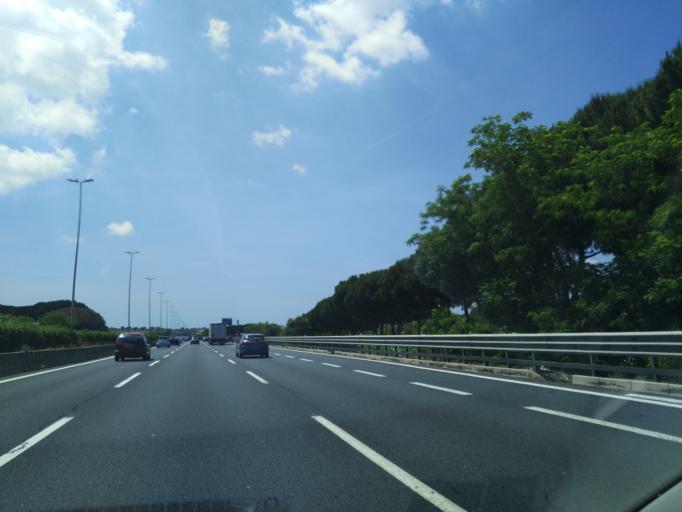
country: IT
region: Latium
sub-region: Citta metropolitana di Roma Capitale
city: Borgo Lotti
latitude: 41.7985
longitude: 12.5396
